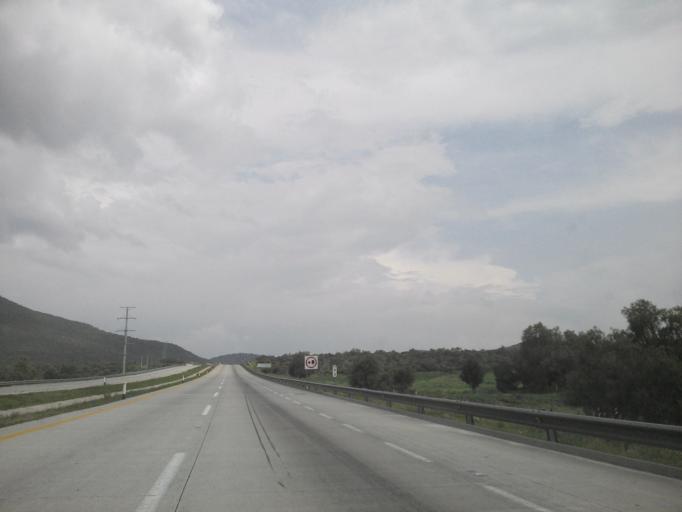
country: MX
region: Hidalgo
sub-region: Atitalaquia
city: Tezoquipa
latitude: 20.0397
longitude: -99.1808
